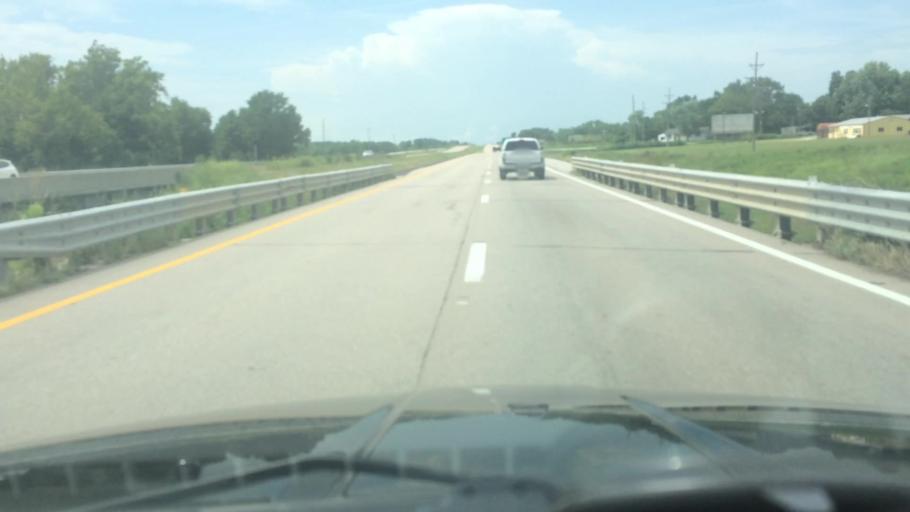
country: US
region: Missouri
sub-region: Polk County
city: Humansville
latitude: 37.7875
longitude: -93.5820
